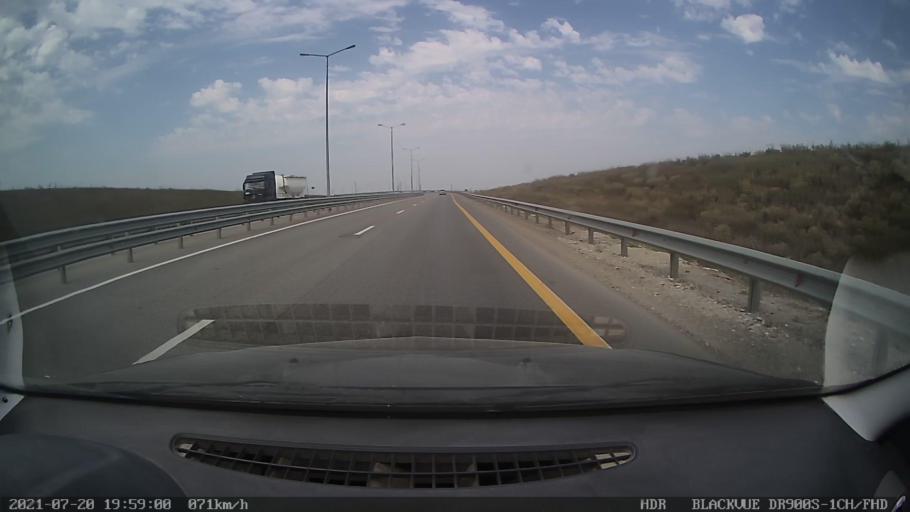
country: RU
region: Krasnodarskiy
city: Taman'
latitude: 45.2001
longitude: 36.7524
